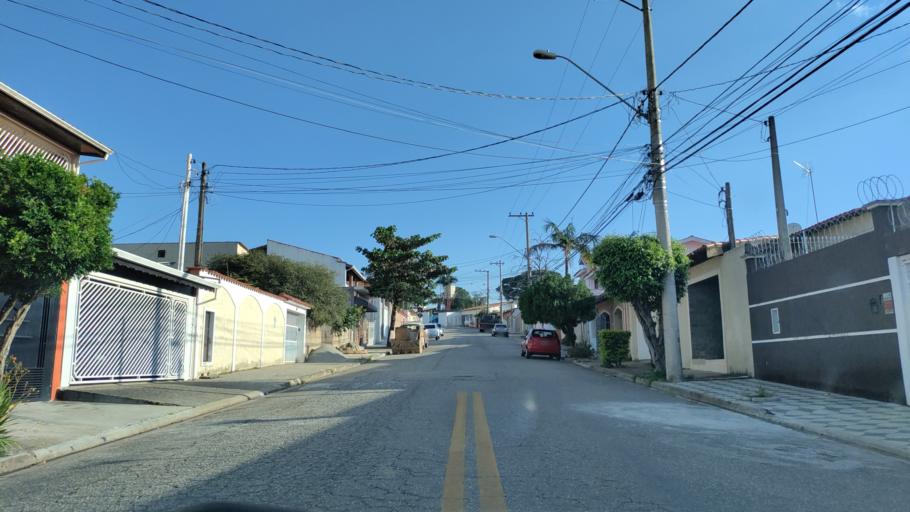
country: BR
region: Sao Paulo
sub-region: Sorocaba
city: Sorocaba
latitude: -23.4750
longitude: -47.4511
